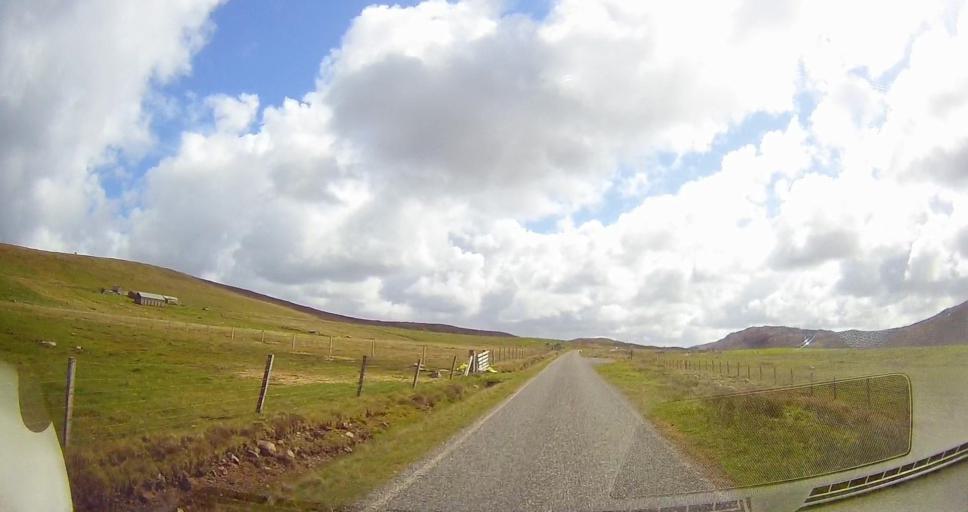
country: GB
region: Scotland
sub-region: Shetland Islands
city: Lerwick
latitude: 60.5692
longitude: -1.3328
